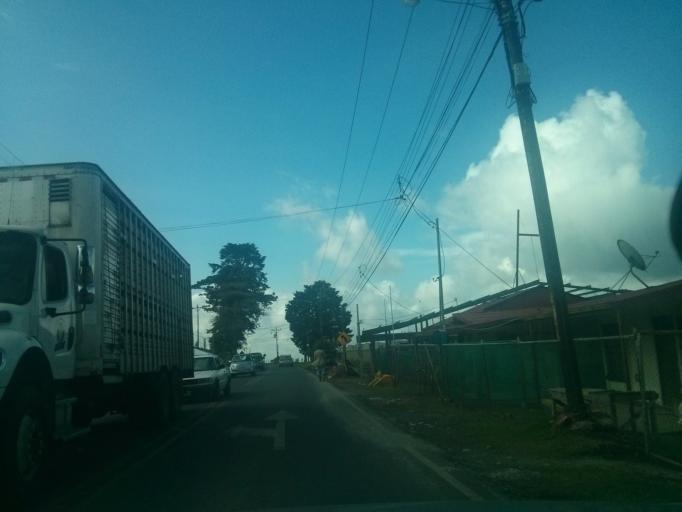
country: CR
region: Heredia
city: Santo Domingo
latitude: 10.1724
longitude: -84.1580
